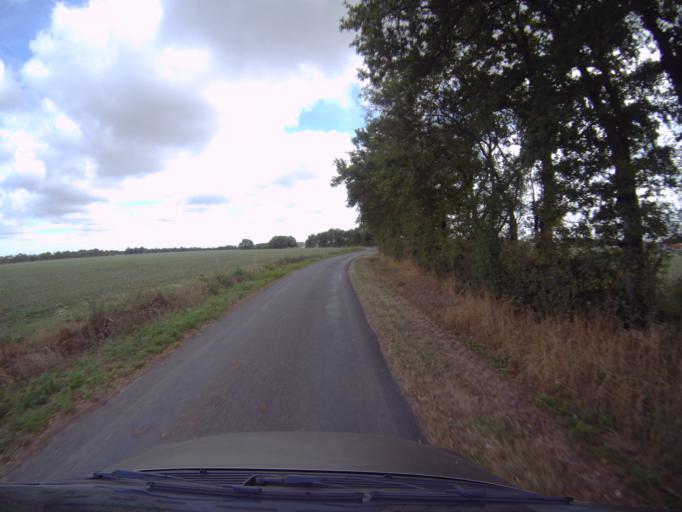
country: FR
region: Pays de la Loire
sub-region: Departement de la Loire-Atlantique
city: La Planche
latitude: 47.0147
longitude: -1.4142
